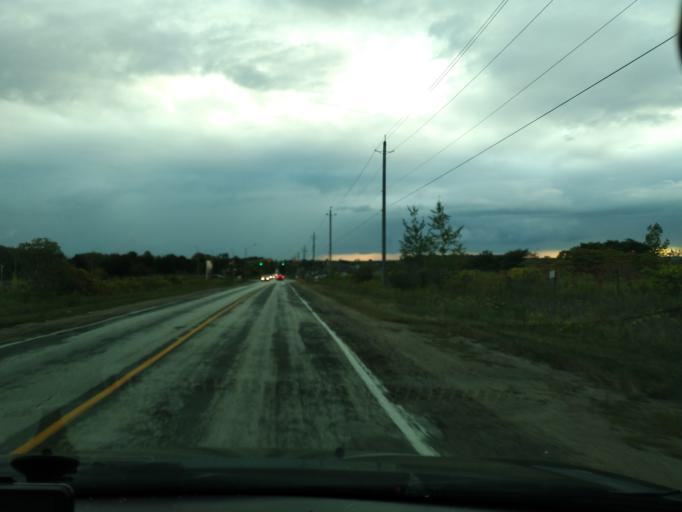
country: CA
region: Ontario
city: Innisfil
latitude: 44.2988
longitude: -79.5610
